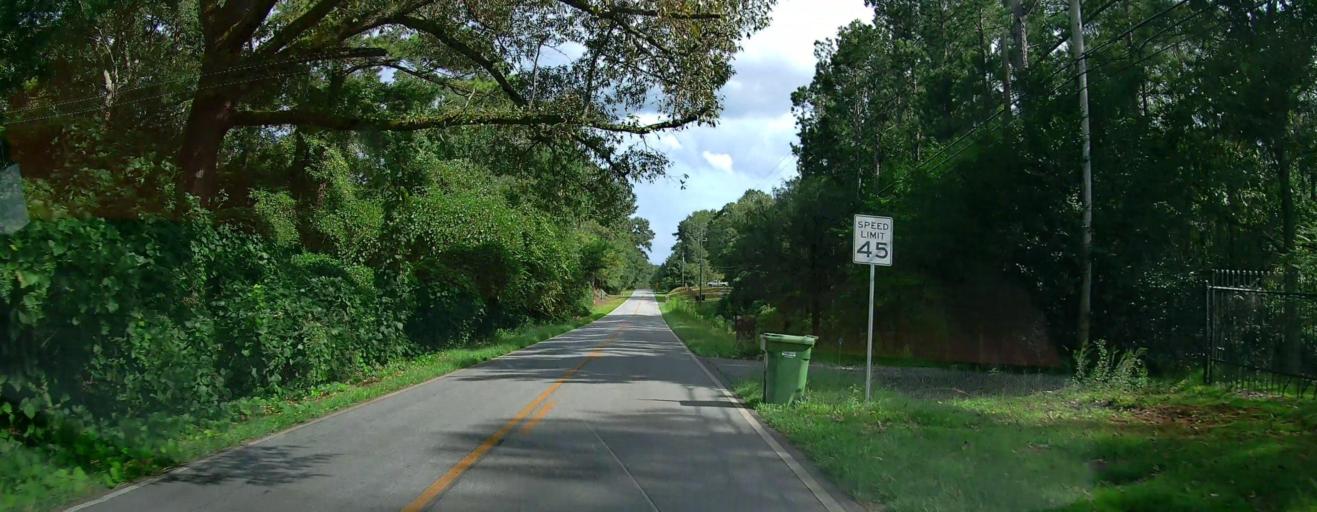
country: US
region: Alabama
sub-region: Russell County
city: Phenix City
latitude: 32.5851
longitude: -84.9770
